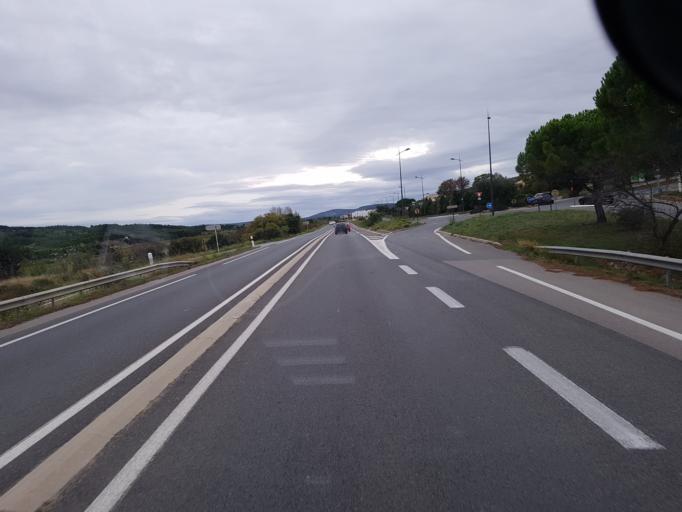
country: FR
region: Languedoc-Roussillon
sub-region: Departement de l'Aude
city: Narbonne
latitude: 43.1389
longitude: 2.9716
